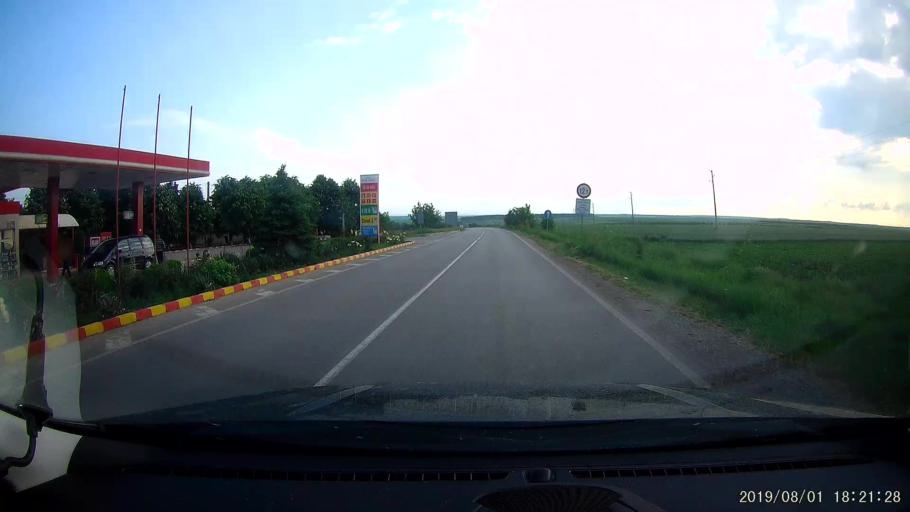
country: BG
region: Shumen
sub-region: Obshtina Kaolinovo
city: Kaolinovo
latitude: 43.6528
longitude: 27.0714
